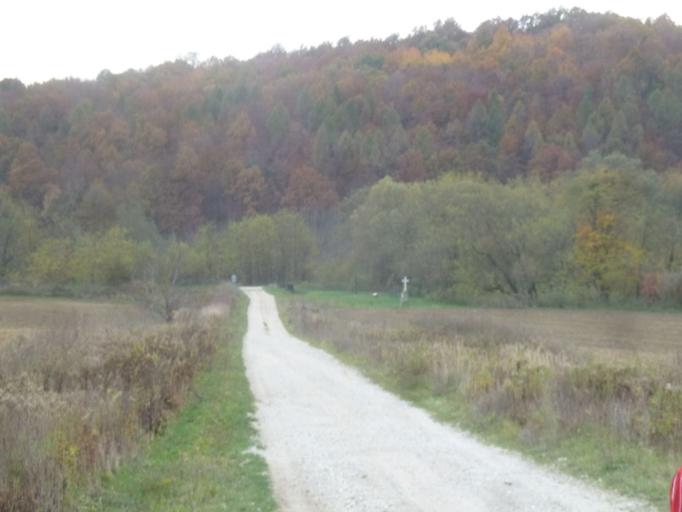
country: HU
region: Zala
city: Pacsa
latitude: 46.6073
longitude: 17.0658
